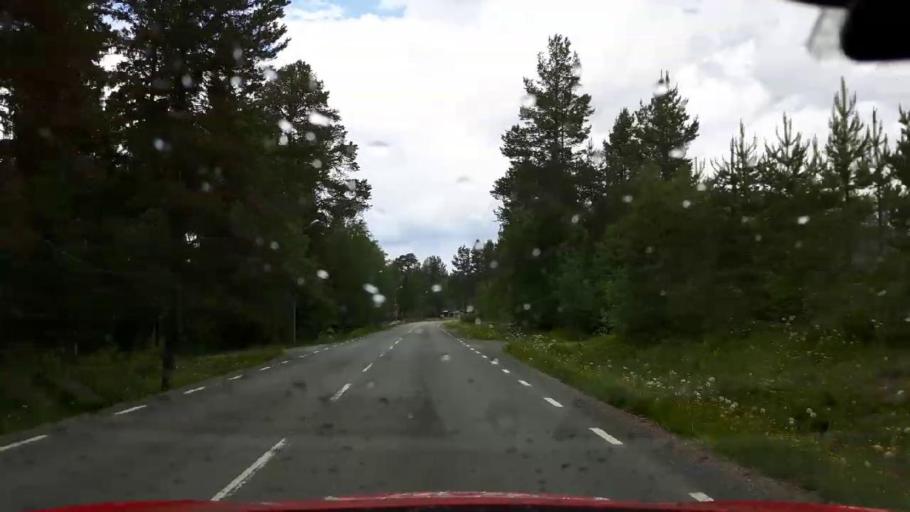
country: SE
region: Jaemtland
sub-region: Krokoms Kommun
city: Krokom
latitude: 63.5643
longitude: 14.2744
